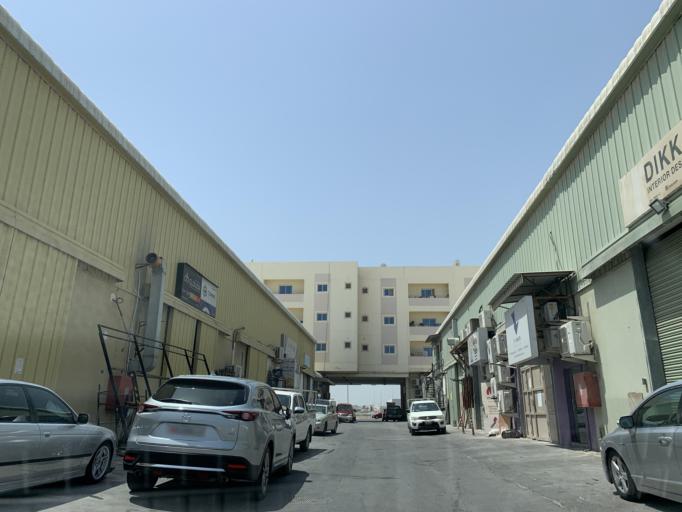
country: BH
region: Northern
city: Madinat `Isa
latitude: 26.1946
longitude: 50.5447
